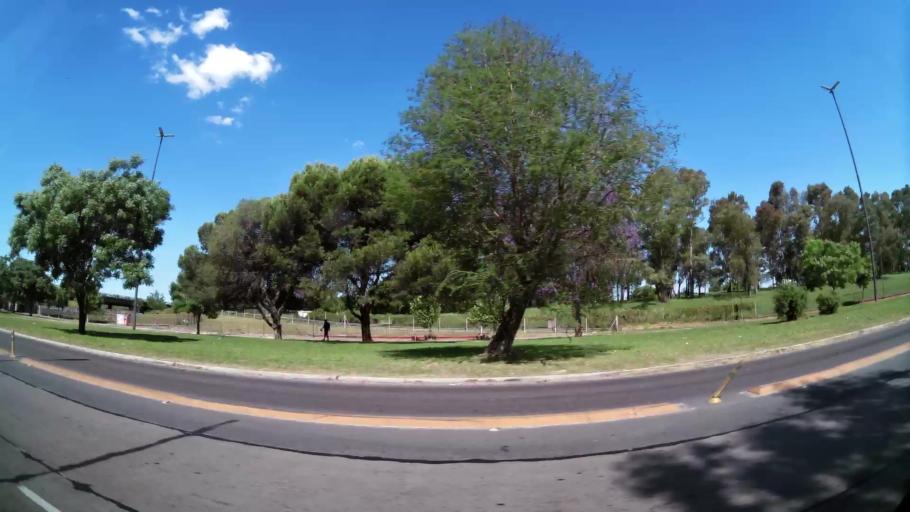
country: AR
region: Buenos Aires F.D.
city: Villa Lugano
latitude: -34.6712
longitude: -58.4451
